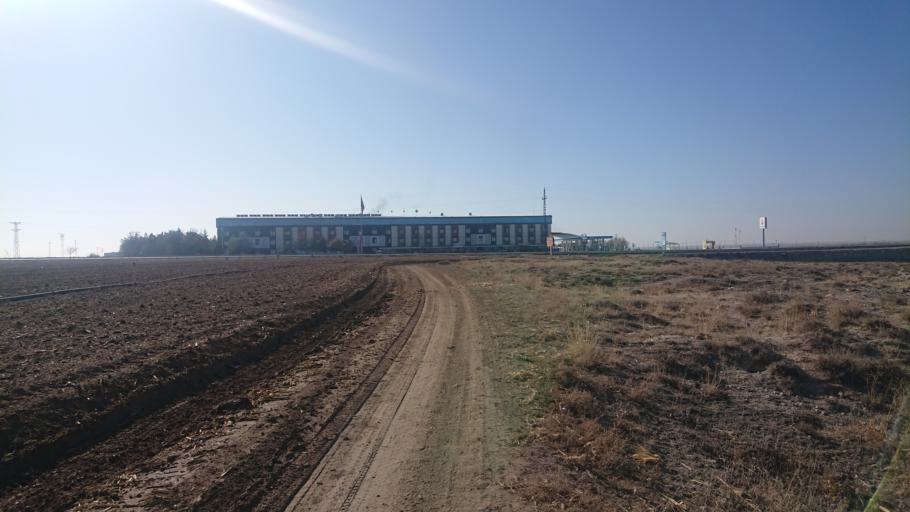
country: TR
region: Aksaray
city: Sultanhani
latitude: 38.2537
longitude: 33.5081
